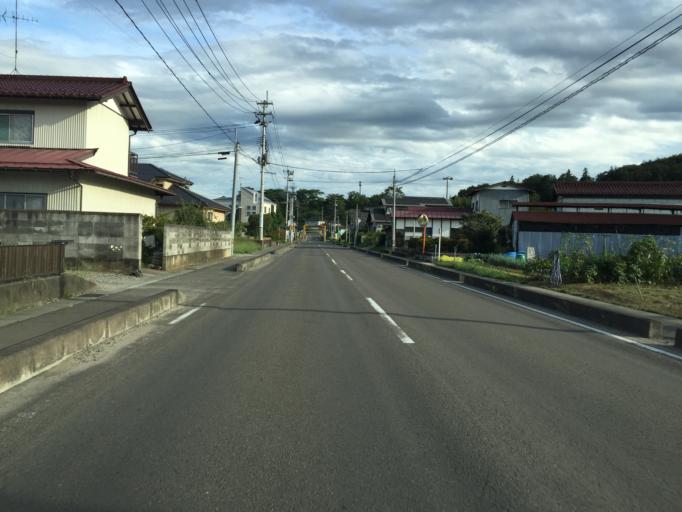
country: JP
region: Fukushima
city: Hobaramachi
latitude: 37.8117
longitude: 140.5426
